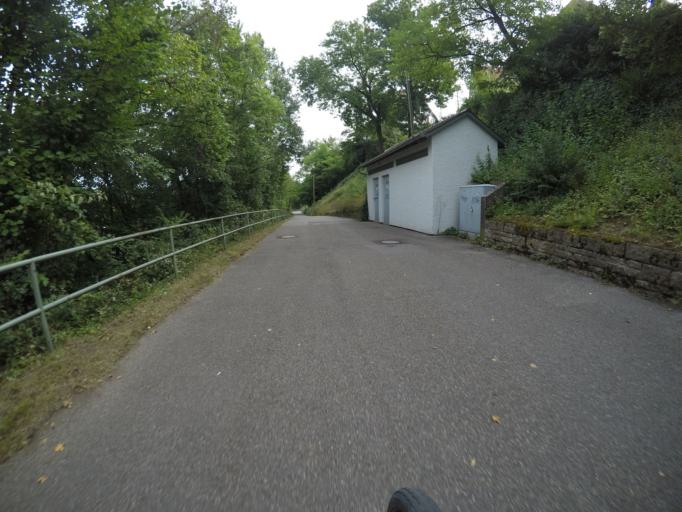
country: DE
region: Baden-Wuerttemberg
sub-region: Regierungsbezirk Stuttgart
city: Stuttgart Muehlhausen
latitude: 48.8379
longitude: 9.2271
